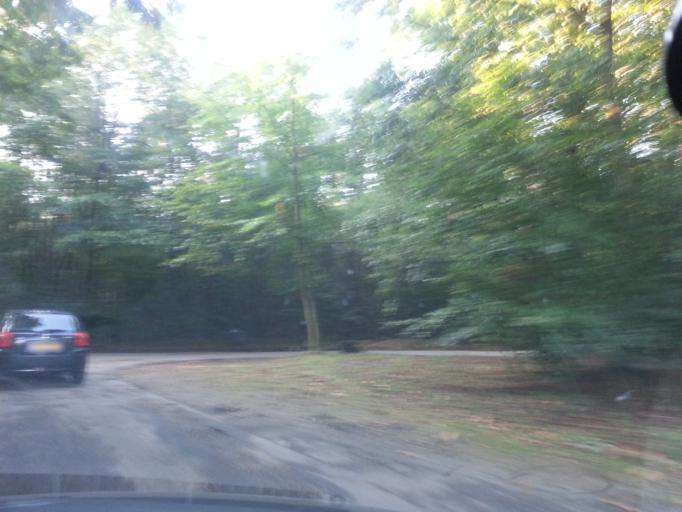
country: NL
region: Utrecht
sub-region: Gemeente Utrechtse Heuvelrug
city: Driebergen-Rijsenburg
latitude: 52.0982
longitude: 5.2780
